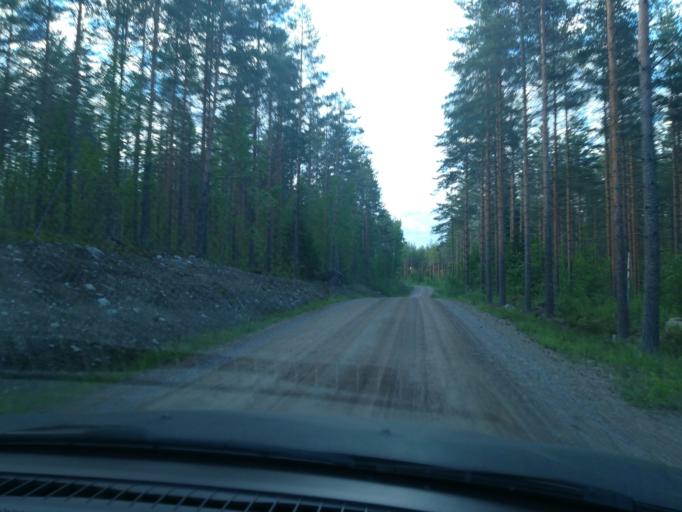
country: FI
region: Southern Savonia
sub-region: Mikkeli
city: Puumala
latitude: 61.5813
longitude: 28.1650
